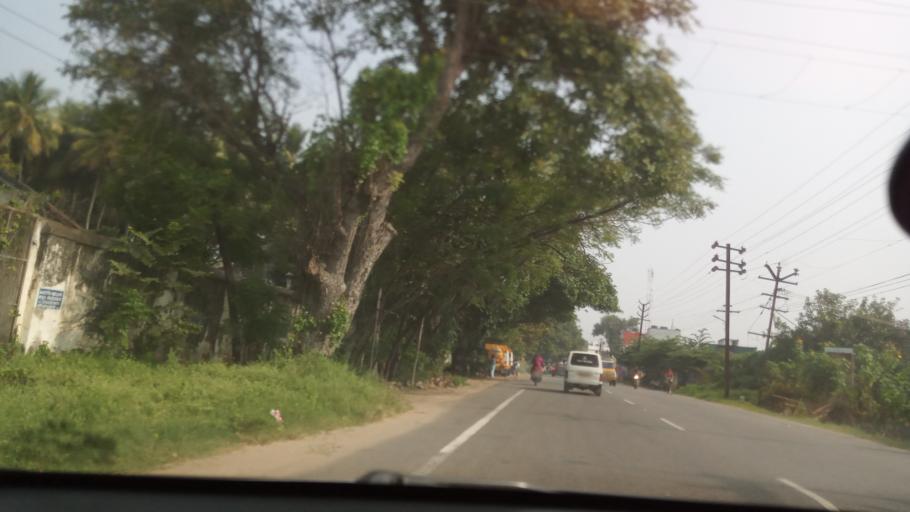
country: IN
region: Tamil Nadu
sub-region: Erode
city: Punjai Puliyampatti
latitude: 11.3464
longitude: 77.1638
